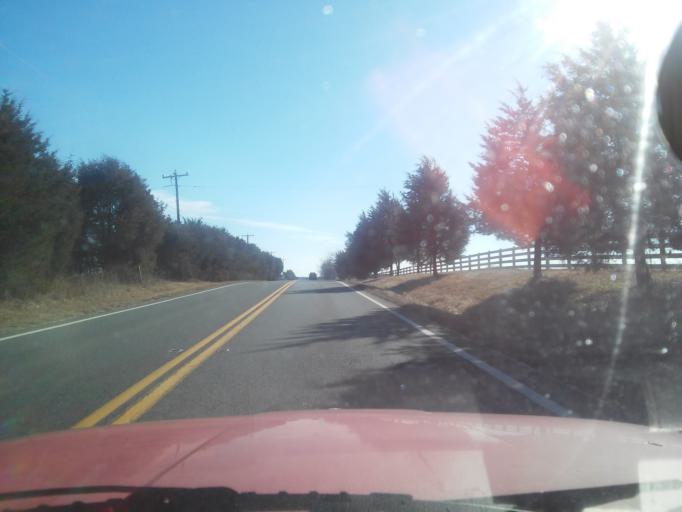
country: US
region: Virginia
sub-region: Orange County
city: Gordonsville
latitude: 38.0383
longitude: -78.1896
